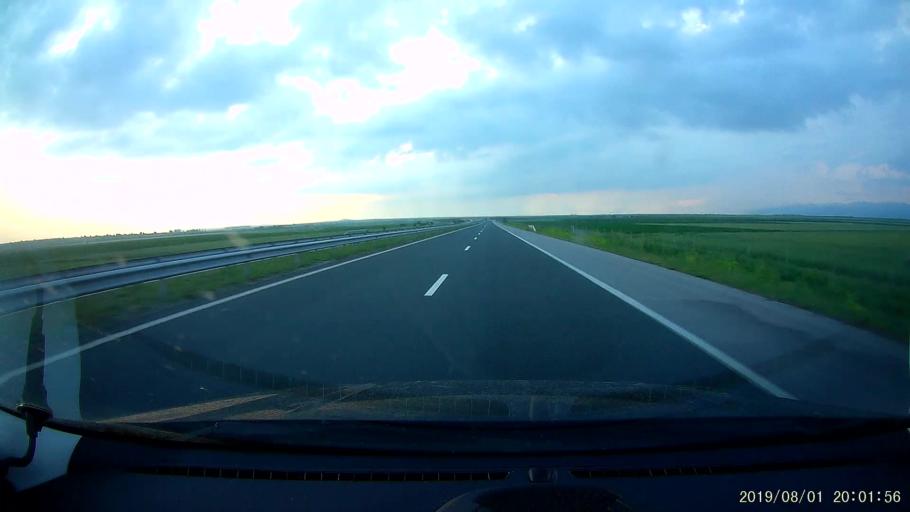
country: BG
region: Yambol
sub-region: Obshtina Straldzha
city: Straldzha
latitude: 42.5574
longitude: 26.6474
